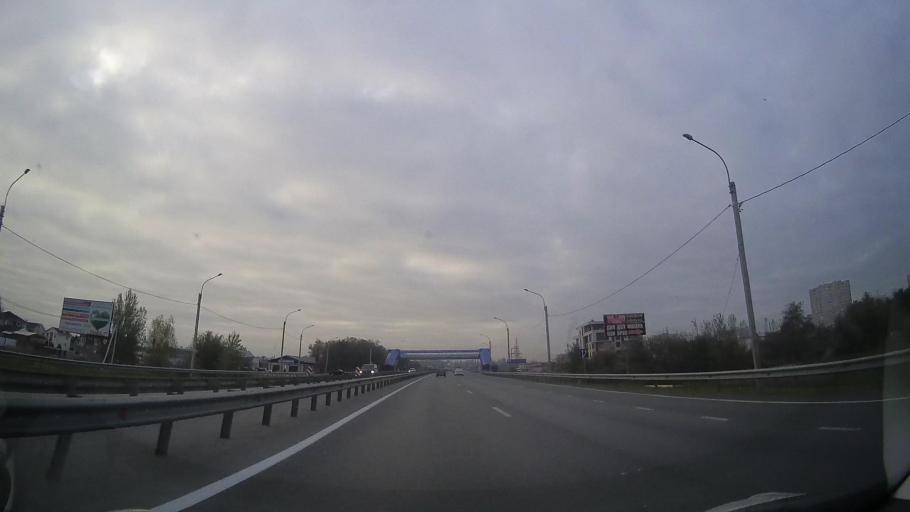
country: RU
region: Rostov
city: Bataysk
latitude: 47.1409
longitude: 39.7760
